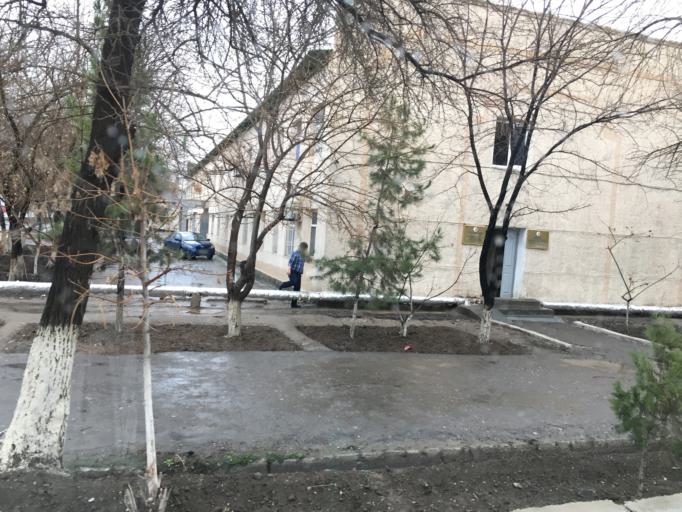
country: TM
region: Mary
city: Mary
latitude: 37.5911
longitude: 61.8280
